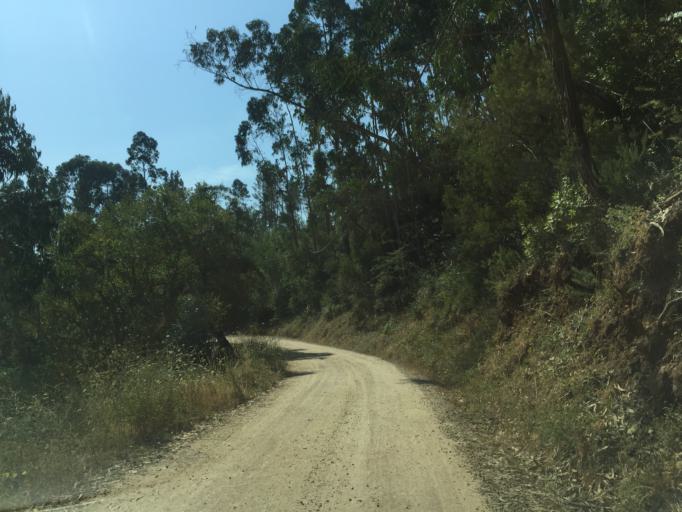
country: PT
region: Santarem
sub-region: Ferreira do Zezere
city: Ferreira do Zezere
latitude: 39.6078
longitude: -8.2785
